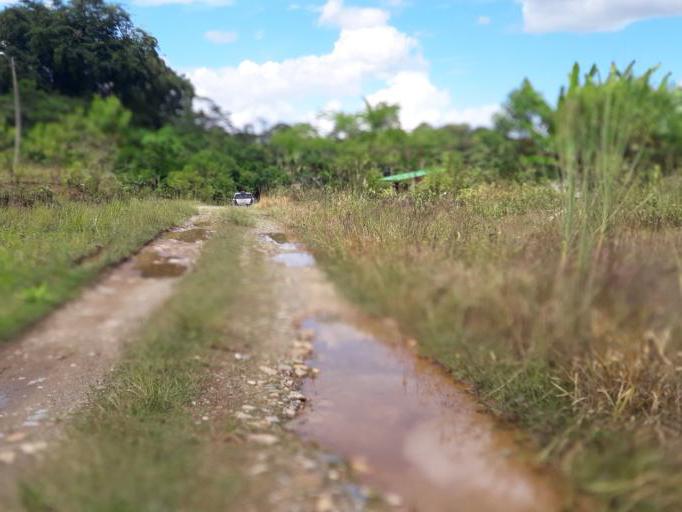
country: EC
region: Napo
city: Tena
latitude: -0.9588
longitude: -77.8172
